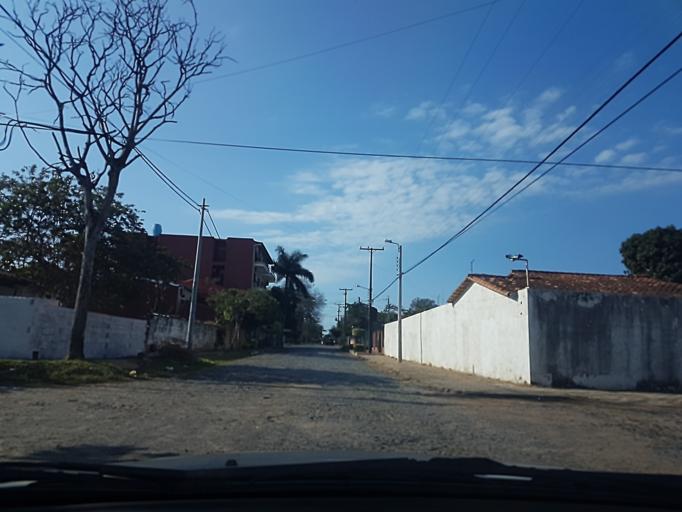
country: PY
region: Central
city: Colonia Mariano Roque Alonso
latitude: -25.2412
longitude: -57.5408
